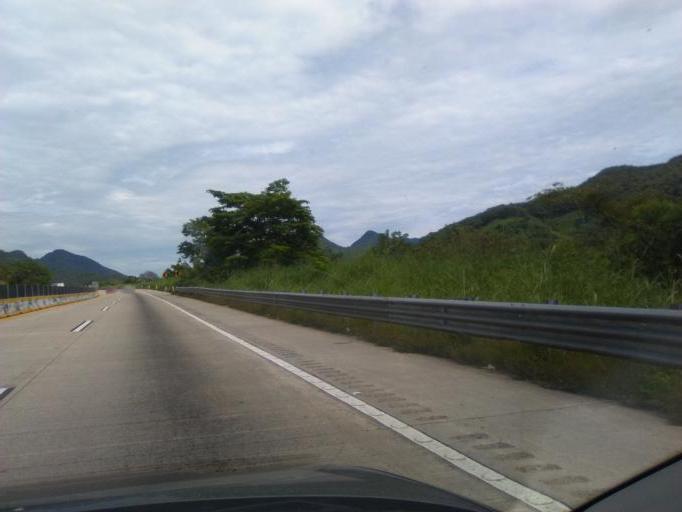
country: MX
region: Guerrero
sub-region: Chilpancingo de los Bravo
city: Julian Blanco (Dos Caminos)
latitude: 17.2131
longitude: -99.5335
